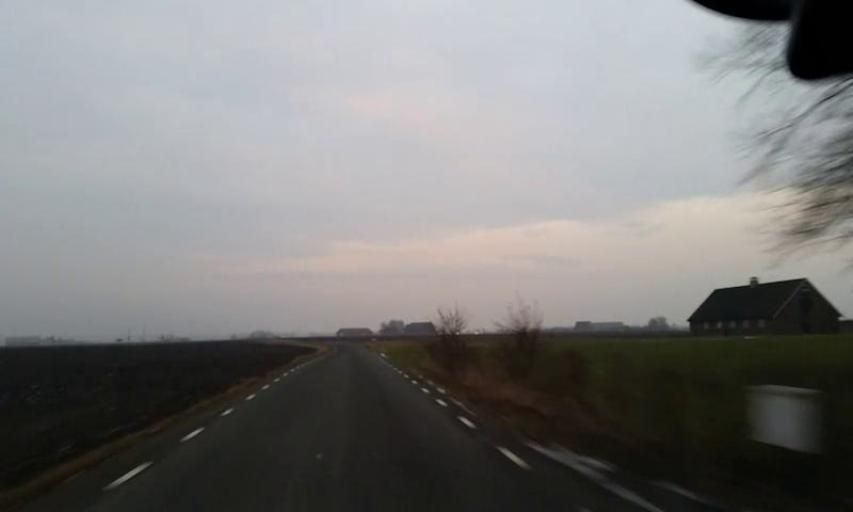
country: SE
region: Skane
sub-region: Angelholms Kommun
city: AEngelholm
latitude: 56.2751
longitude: 12.8797
